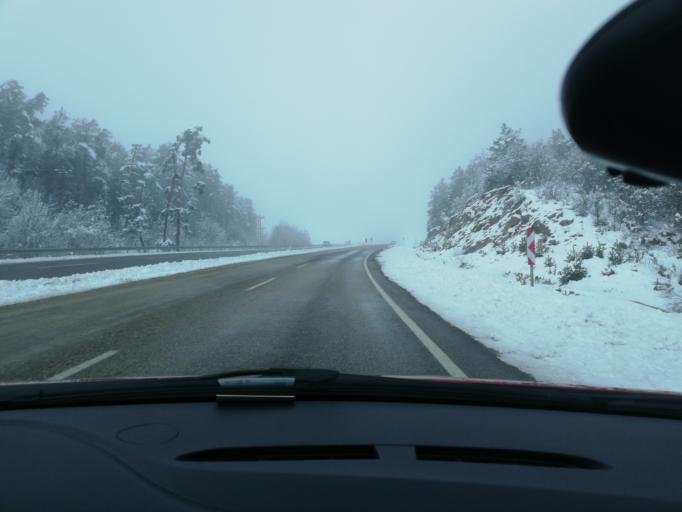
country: TR
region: Kastamonu
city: Akkaya
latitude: 41.2992
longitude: 33.5281
